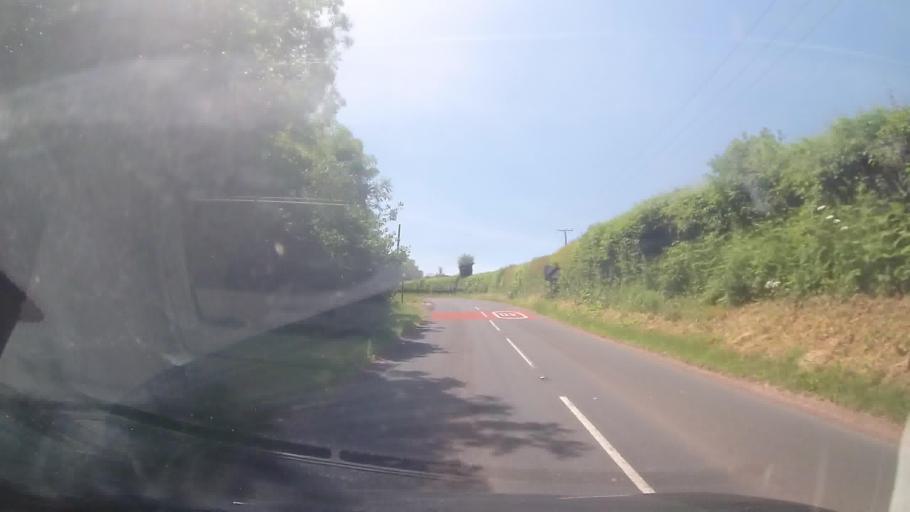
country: GB
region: England
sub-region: Herefordshire
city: Llanrothal
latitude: 51.8823
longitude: -2.7331
